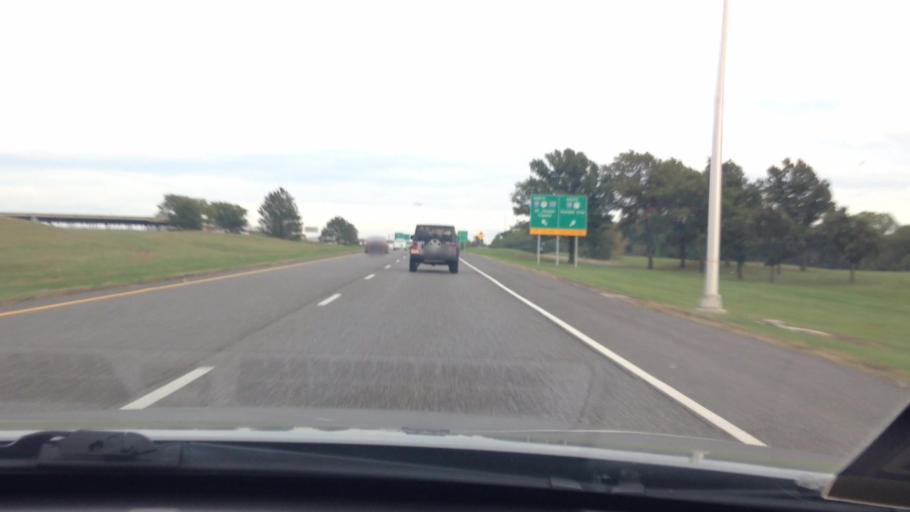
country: US
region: Missouri
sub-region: Platte County
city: Weatherby Lake
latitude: 39.3108
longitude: -94.6977
